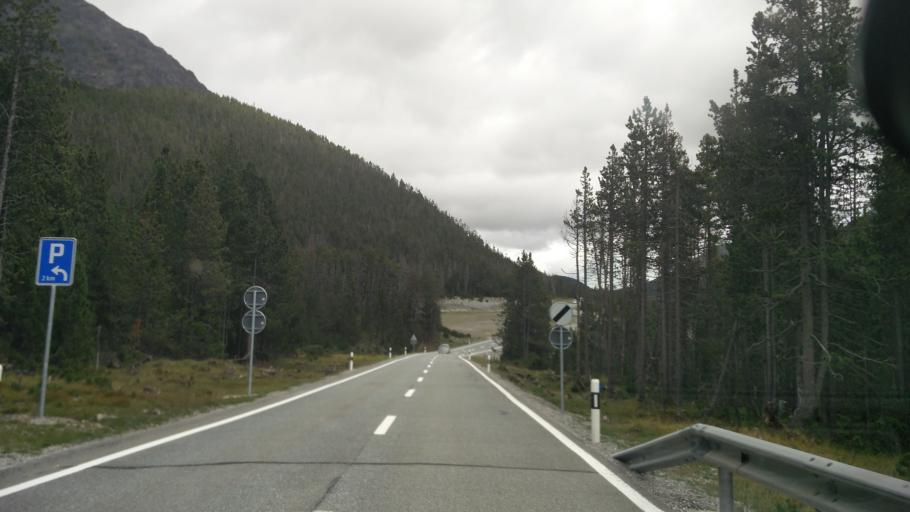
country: CH
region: Grisons
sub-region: Inn District
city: Zernez
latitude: 46.6585
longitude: 10.2407
